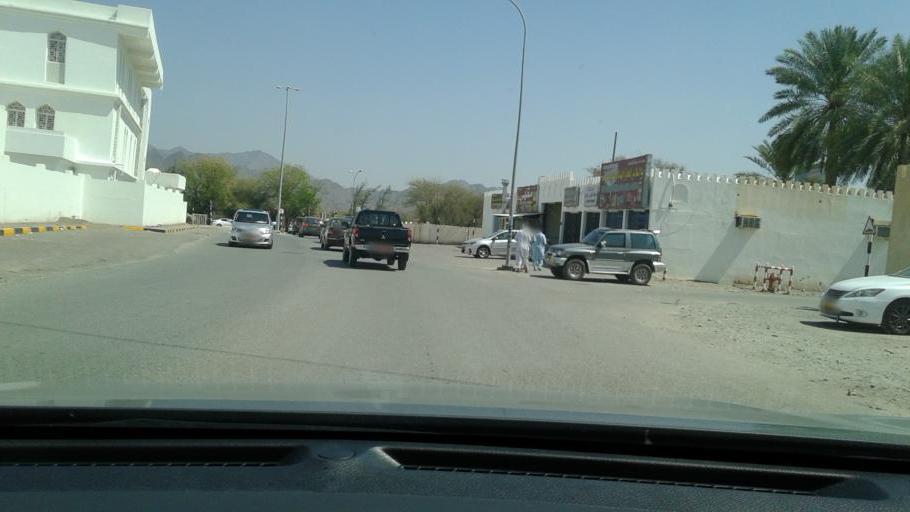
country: OM
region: Al Batinah
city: Rustaq
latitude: 23.3995
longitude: 57.4193
